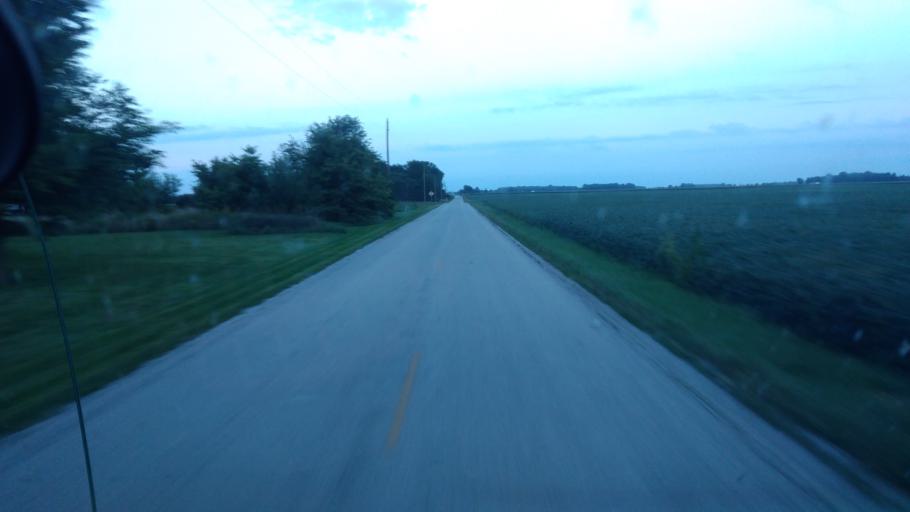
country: US
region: Ohio
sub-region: Hardin County
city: Kenton
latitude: 40.6729
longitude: -83.5317
